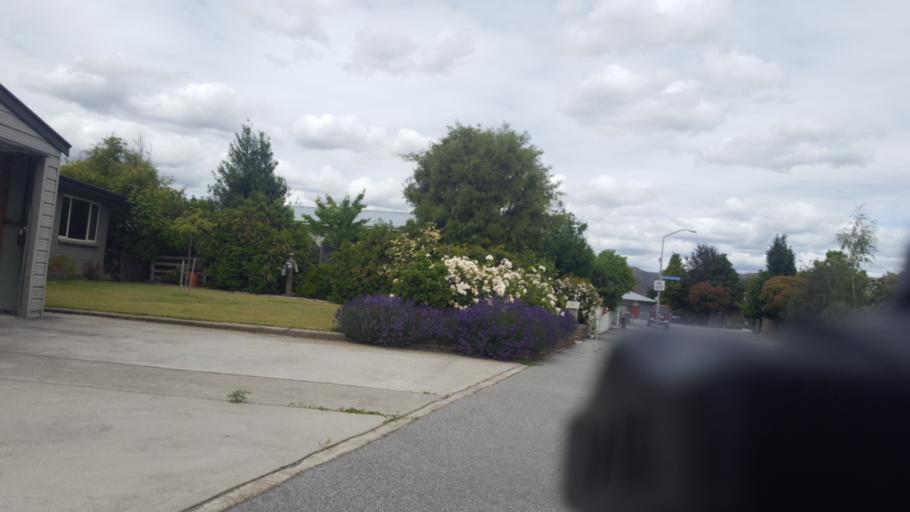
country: NZ
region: Otago
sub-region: Queenstown-Lakes District
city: Wanaka
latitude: -45.2458
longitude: 169.3811
